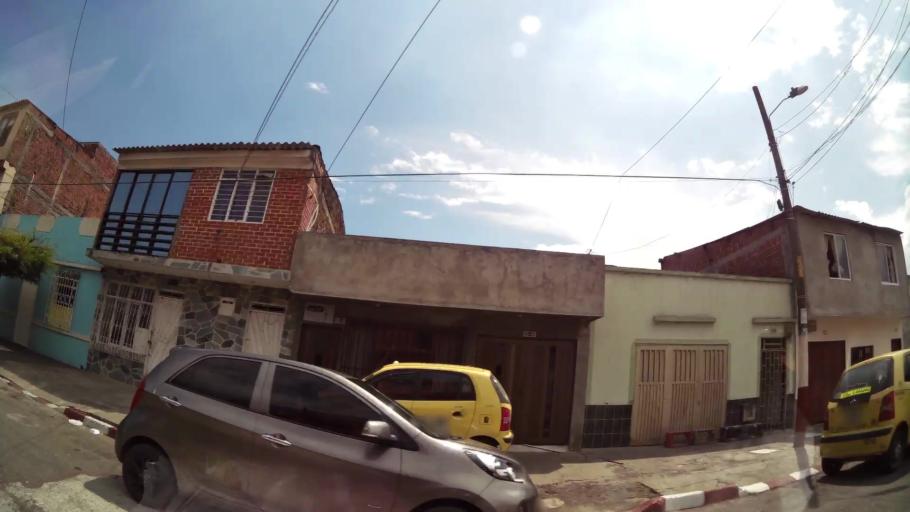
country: CO
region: Valle del Cauca
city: Cali
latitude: 3.4437
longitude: -76.5157
